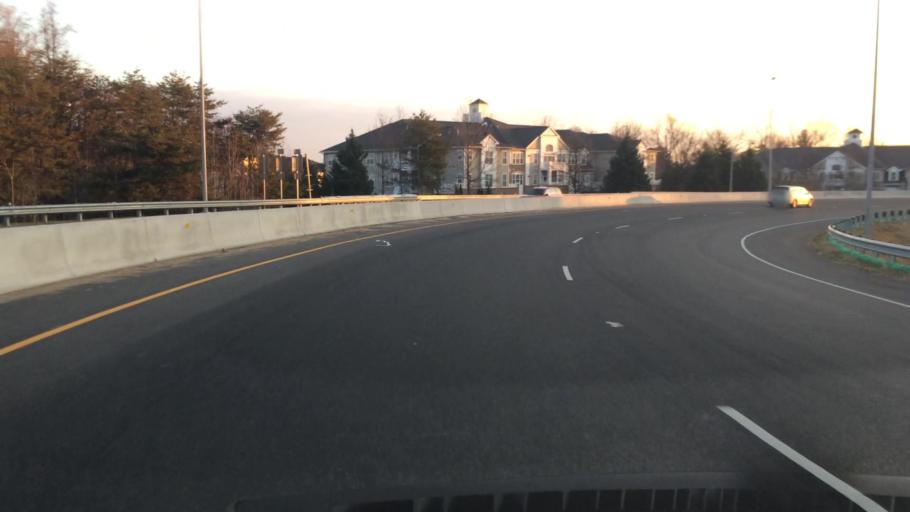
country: US
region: Virginia
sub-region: Fairfax County
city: West Springfield
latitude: 38.7611
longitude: -77.2176
